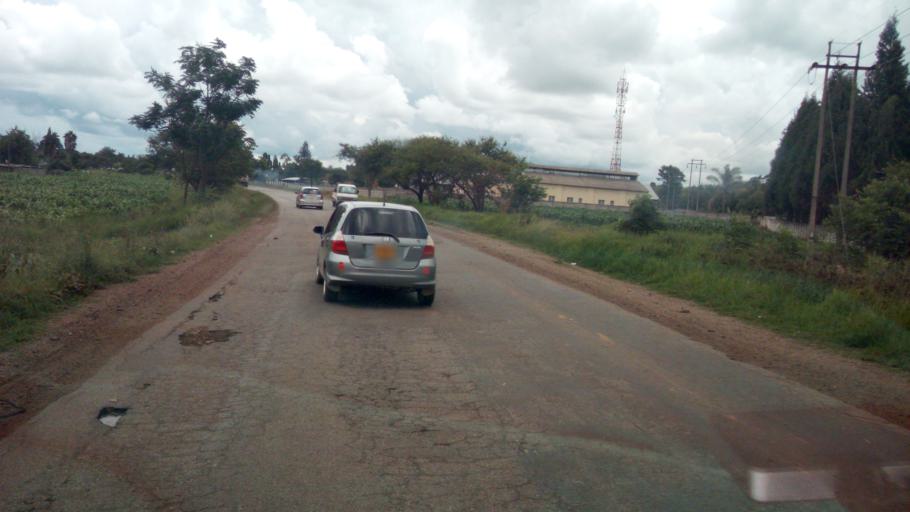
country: ZW
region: Harare
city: Harare
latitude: -17.7800
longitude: 30.9951
